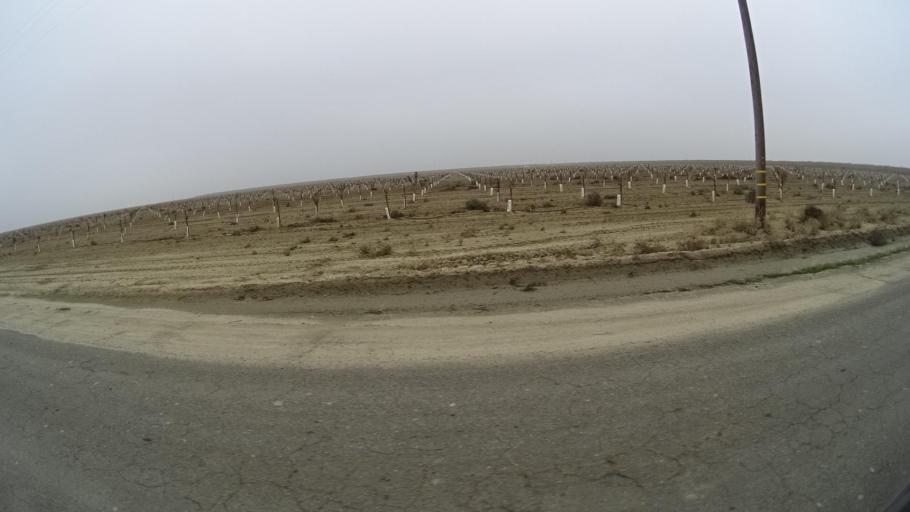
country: US
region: California
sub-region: Kern County
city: Wasco
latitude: 35.6905
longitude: -119.4196
